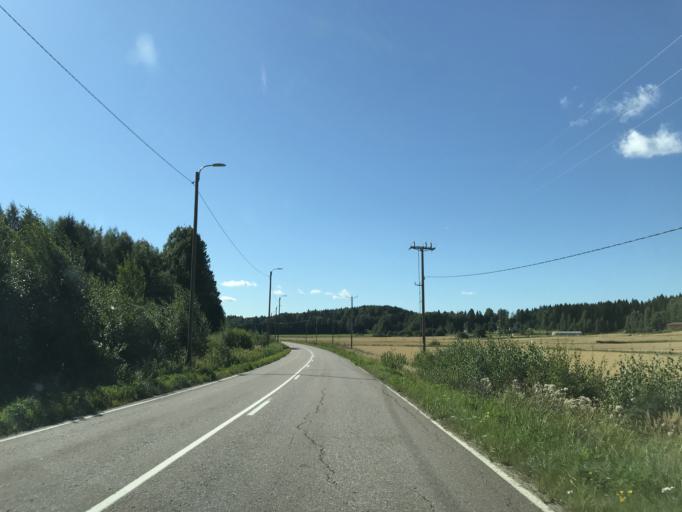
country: FI
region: Uusimaa
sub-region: Helsinki
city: Nurmijaervi
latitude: 60.4908
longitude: 24.6244
